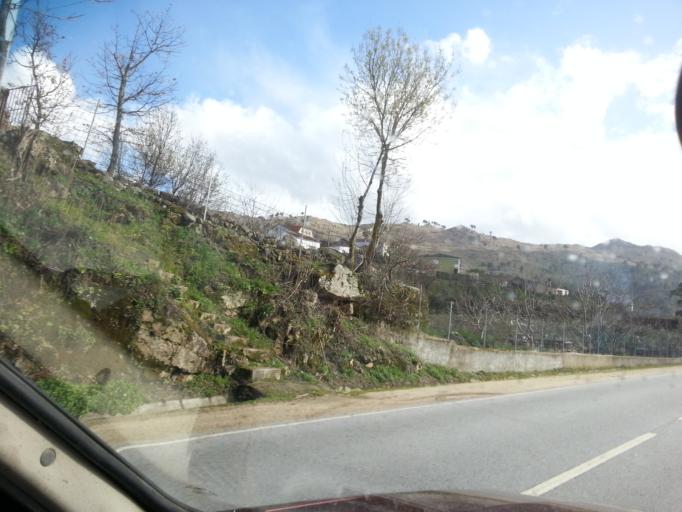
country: PT
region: Guarda
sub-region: Guarda
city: Guarda
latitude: 40.5912
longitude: -7.2898
